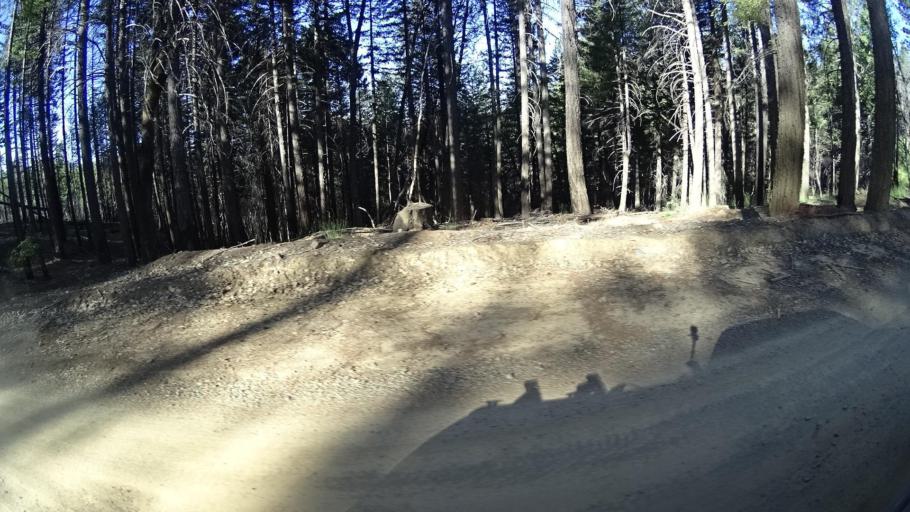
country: US
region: California
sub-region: Lake County
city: Upper Lake
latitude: 39.3561
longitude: -122.9816
